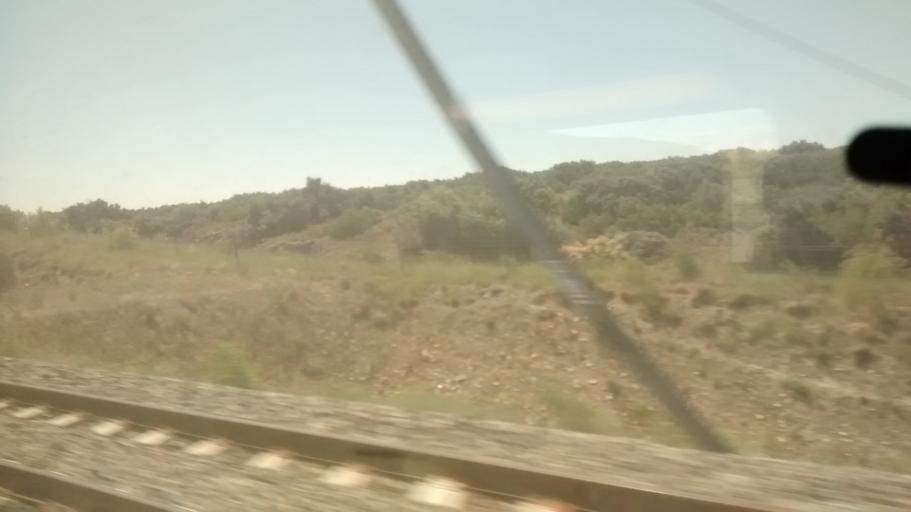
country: FR
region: Languedoc-Roussillon
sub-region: Departement du Gard
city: Pujaut
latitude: 44.0178
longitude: 4.7419
